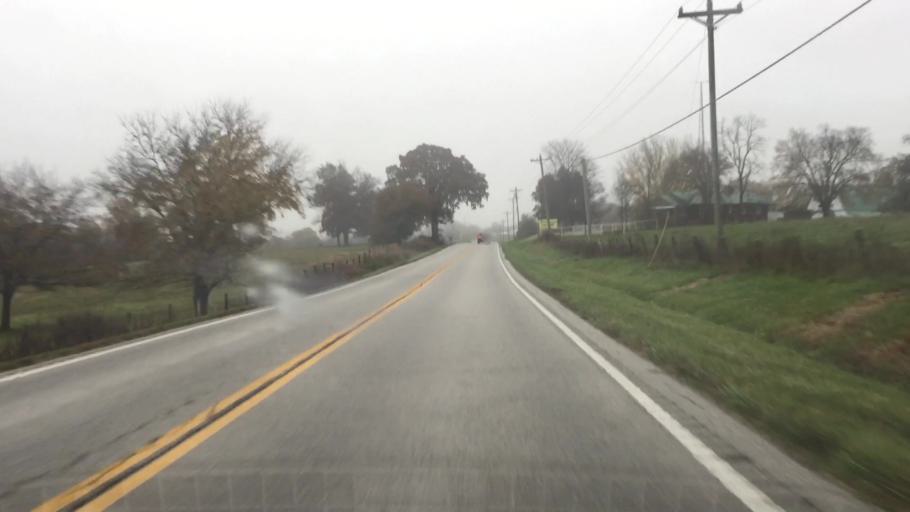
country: US
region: Missouri
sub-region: Callaway County
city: Fulton
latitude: 38.8626
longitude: -92.0052
